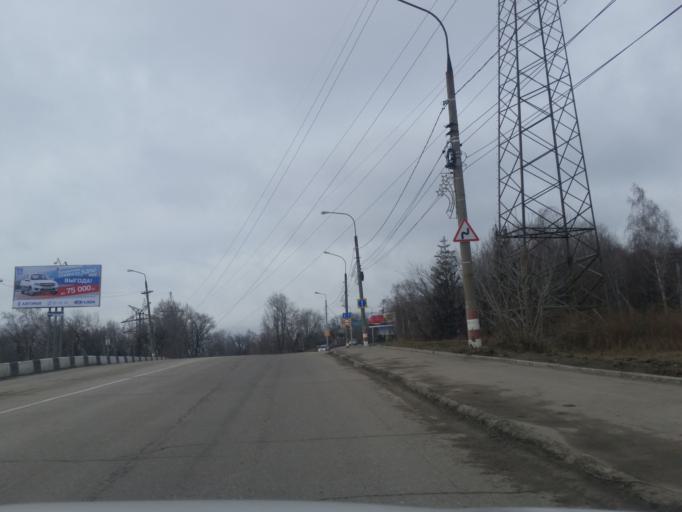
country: RU
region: Ulyanovsk
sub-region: Ulyanovskiy Rayon
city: Ulyanovsk
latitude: 54.3101
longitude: 48.4099
